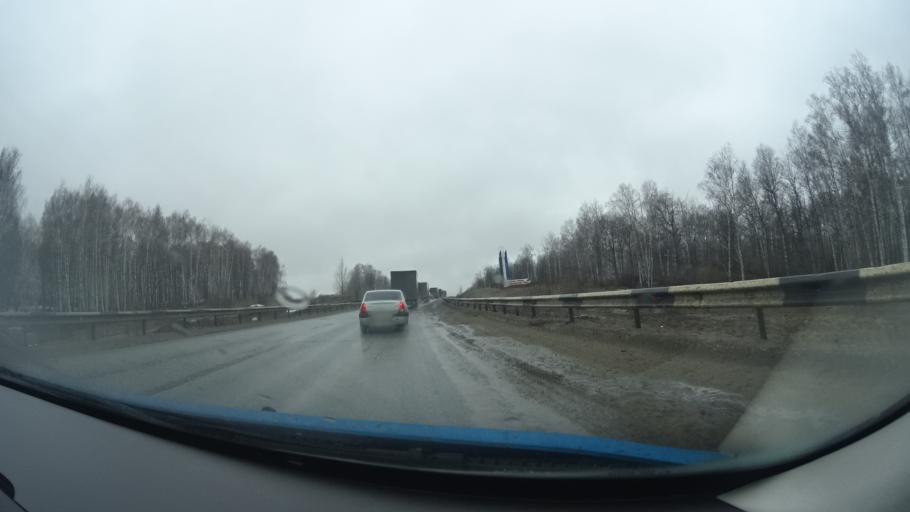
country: RU
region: Bashkortostan
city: Kandry
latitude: 54.5920
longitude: 54.2778
